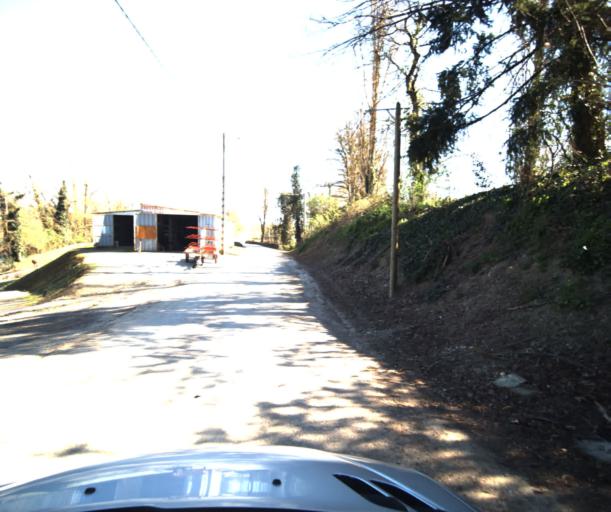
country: FR
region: Midi-Pyrenees
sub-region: Departement du Tarn-et-Garonne
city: Bressols
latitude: 43.9679
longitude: 1.3409
